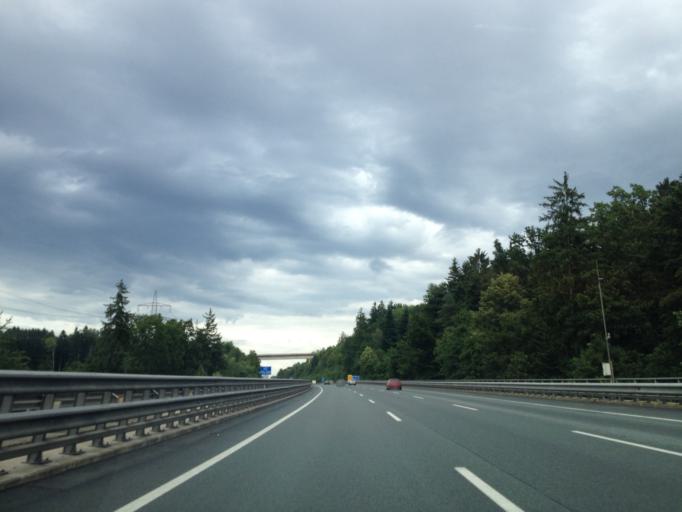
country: AT
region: Styria
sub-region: Politischer Bezirk Weiz
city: Nitscha
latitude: 47.0950
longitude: 15.7458
